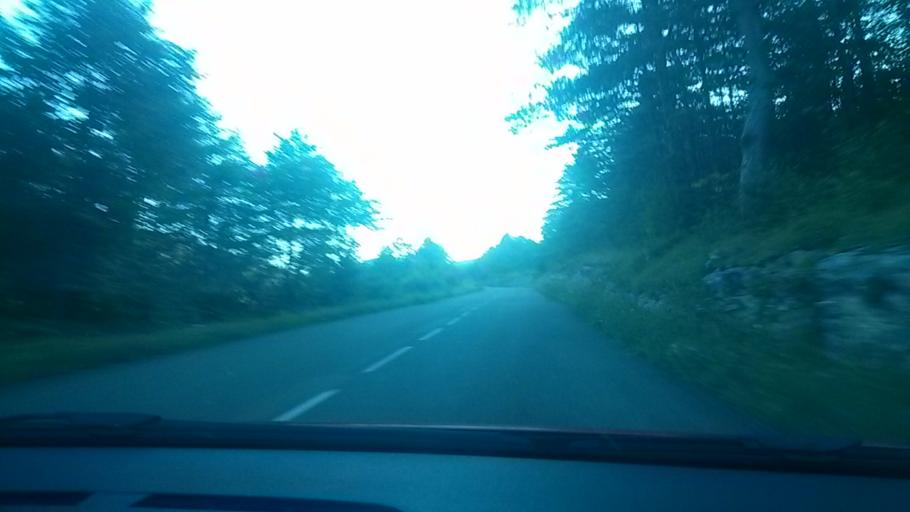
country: FR
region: Franche-Comte
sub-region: Departement du Jura
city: Saint-Claude
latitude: 46.3469
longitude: 5.8352
